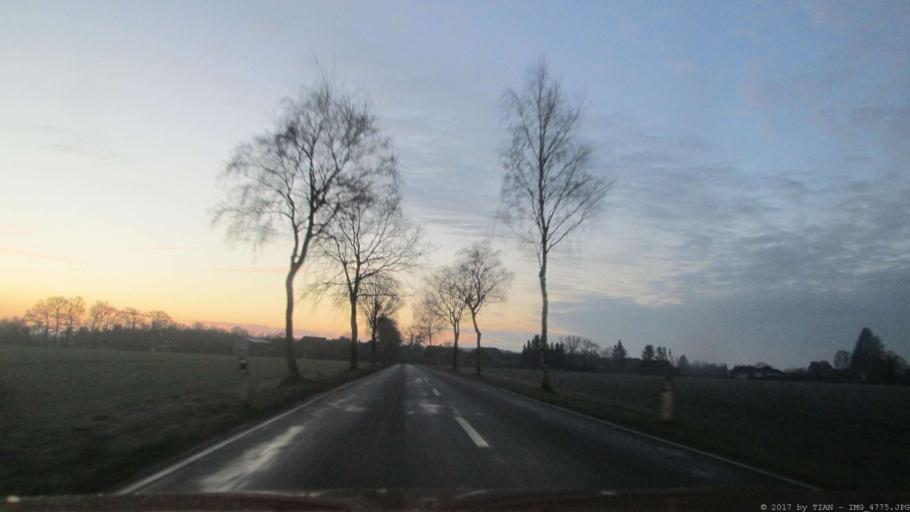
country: DE
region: Lower Saxony
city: Wittingen
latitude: 52.6706
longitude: 10.7993
